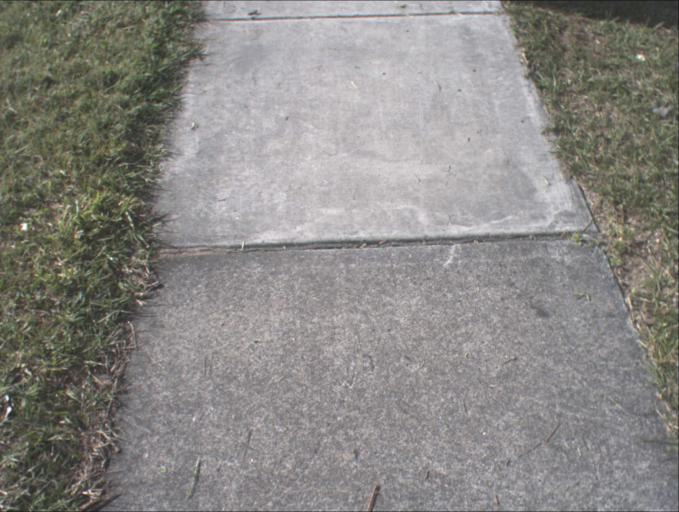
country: AU
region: Queensland
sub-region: Logan
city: Park Ridge South
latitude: -27.6852
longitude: 153.0498
